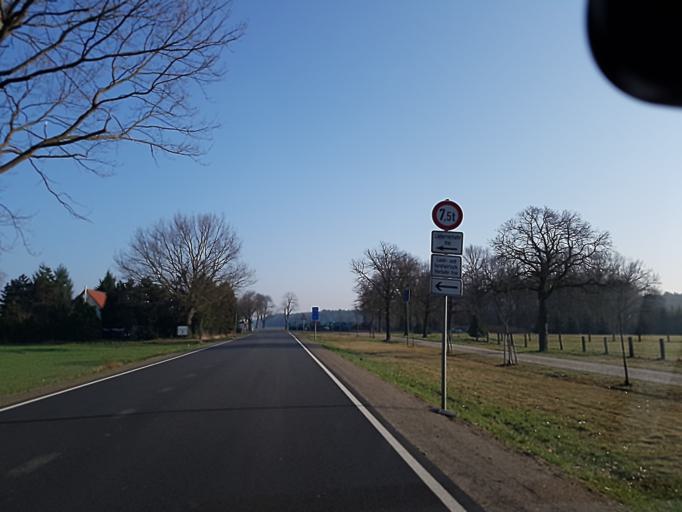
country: DE
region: Brandenburg
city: Bronkow
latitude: 51.6717
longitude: 13.9133
